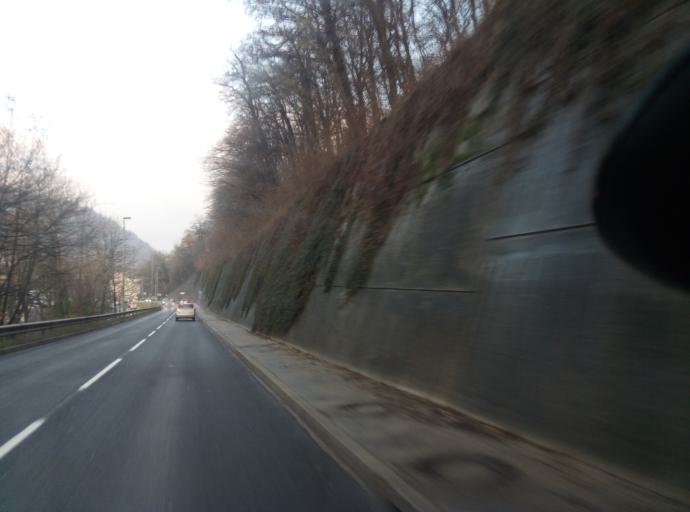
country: SI
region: Kranj
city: Kranj
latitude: 46.2331
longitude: 14.3602
